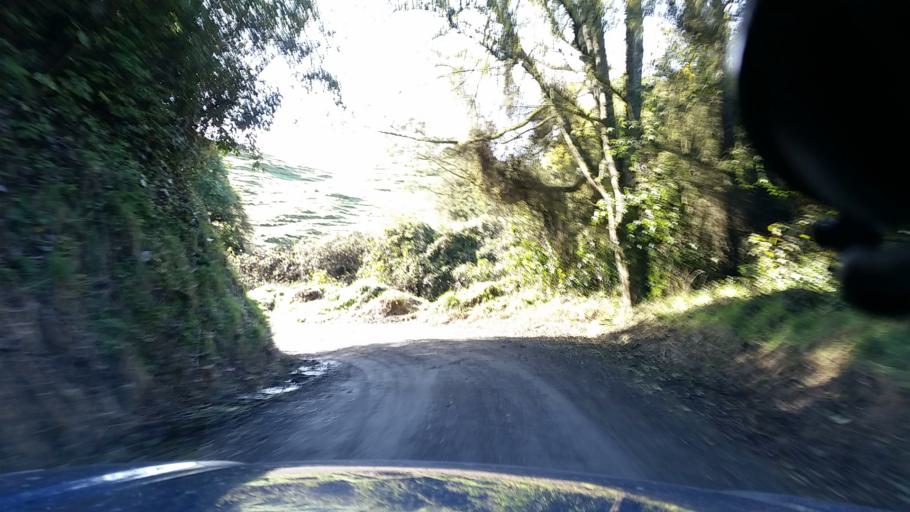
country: NZ
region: Taranaki
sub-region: New Plymouth District
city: Waitara
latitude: -39.0616
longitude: 174.7895
